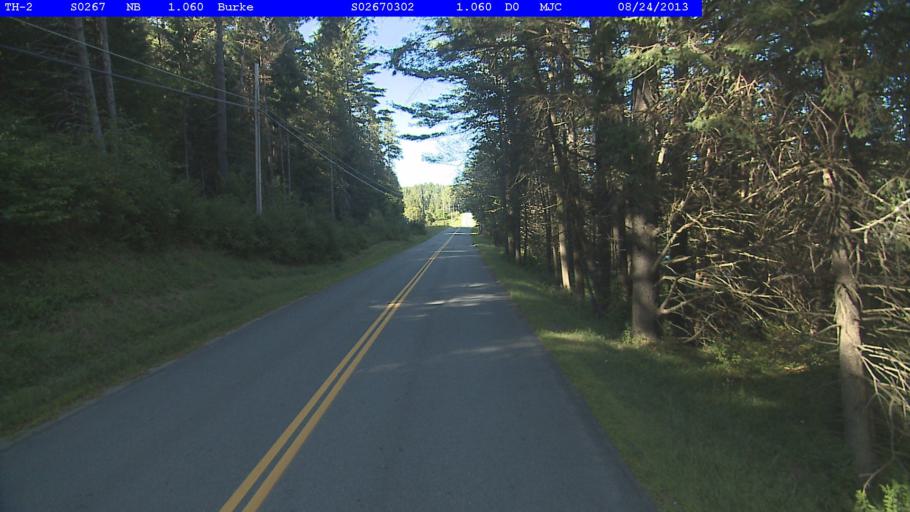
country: US
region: Vermont
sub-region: Caledonia County
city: Lyndonville
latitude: 44.6018
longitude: -71.9403
